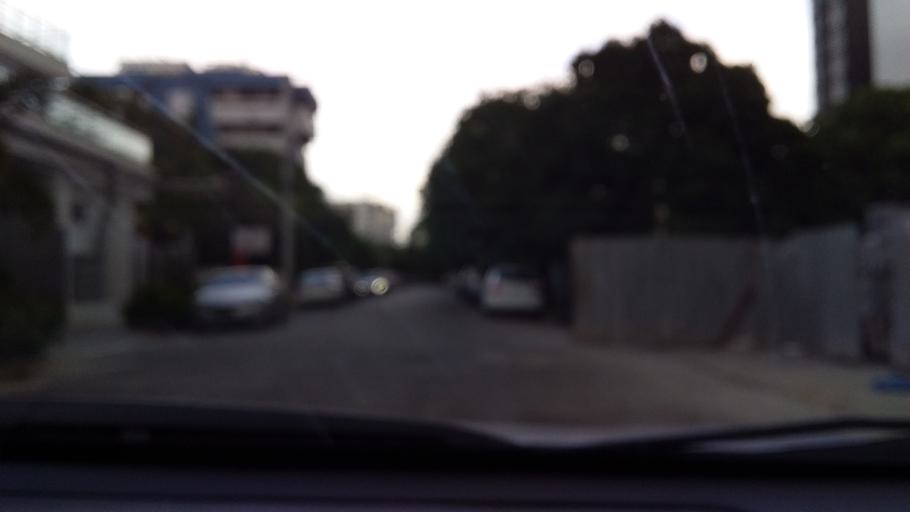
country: DO
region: Nacional
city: La Julia
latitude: 18.4588
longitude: -69.9344
